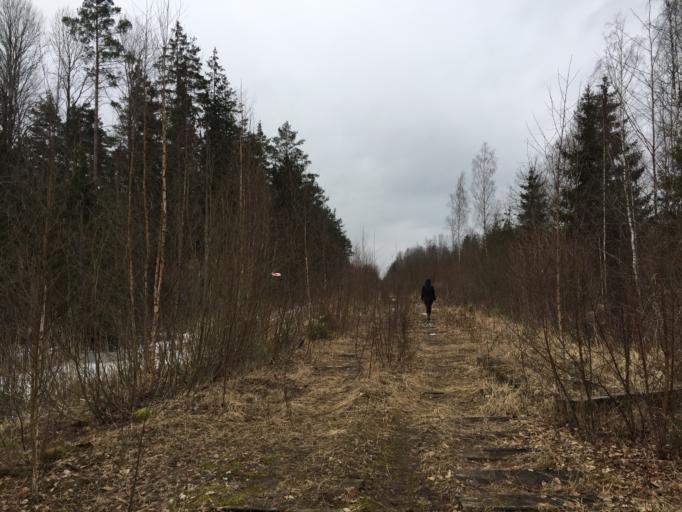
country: LV
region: Lielvarde
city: Lielvarde
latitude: 56.7633
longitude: 24.8193
